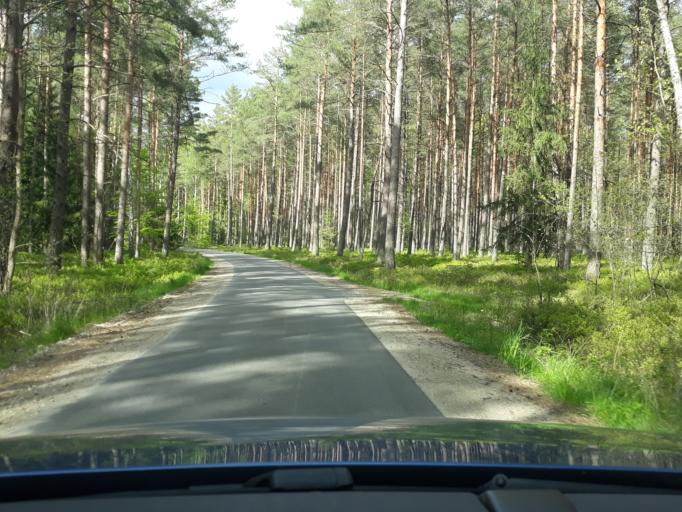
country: PL
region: Pomeranian Voivodeship
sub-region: Powiat czluchowski
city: Czluchow
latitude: 53.7291
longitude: 17.3436
